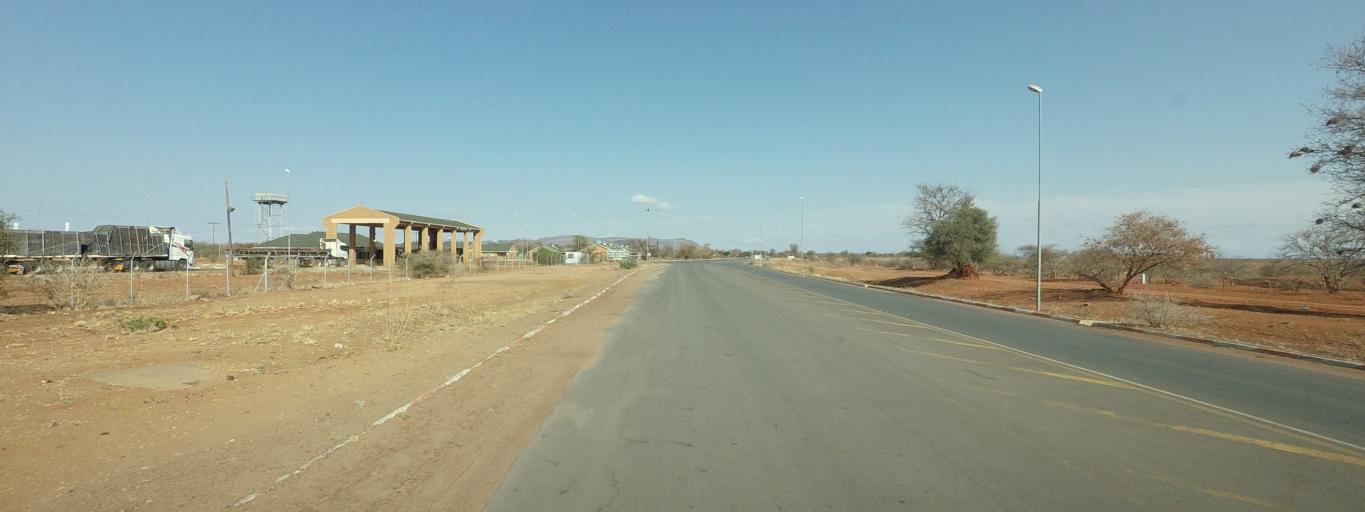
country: BW
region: Central
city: Makobeng
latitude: -22.9942
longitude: 27.9322
